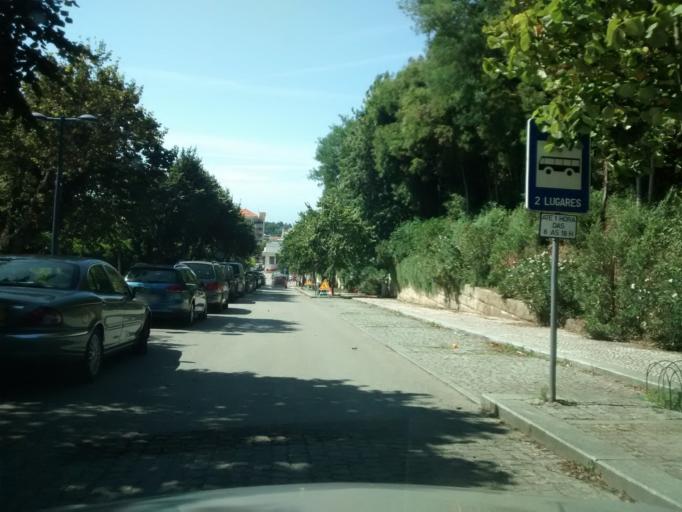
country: PT
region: Aveiro
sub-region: Mealhada
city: Pampilhosa do Botao
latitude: 40.3825
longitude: -8.3746
